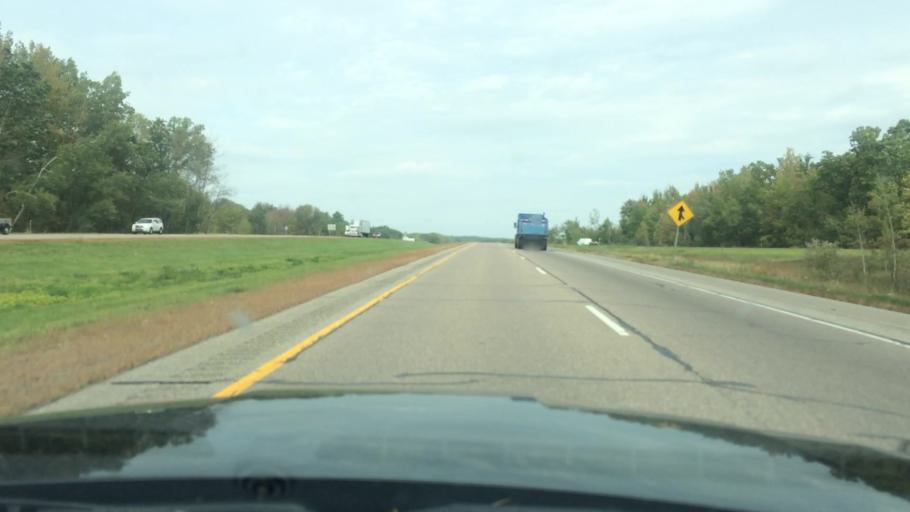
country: US
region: Wisconsin
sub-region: Marathon County
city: Mosinee
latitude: 44.6764
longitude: -89.6417
